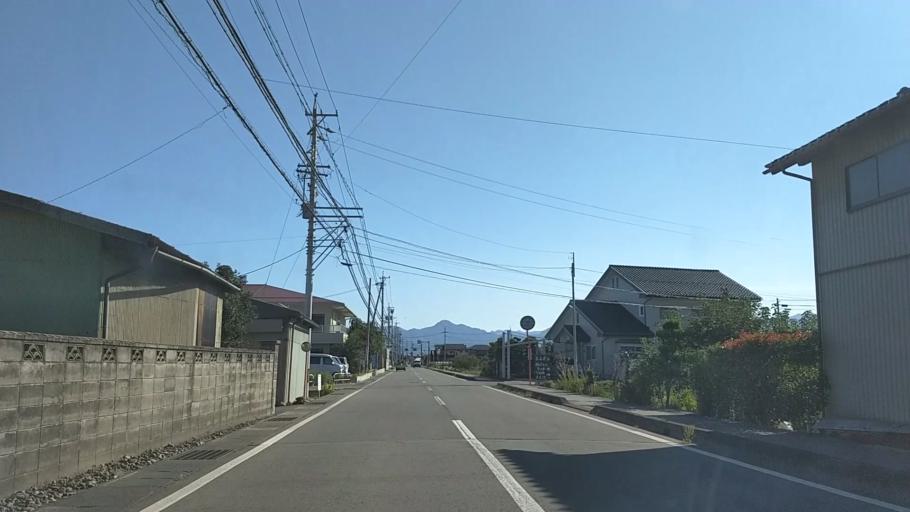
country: JP
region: Nagano
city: Nagano-shi
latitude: 36.6031
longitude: 138.1425
